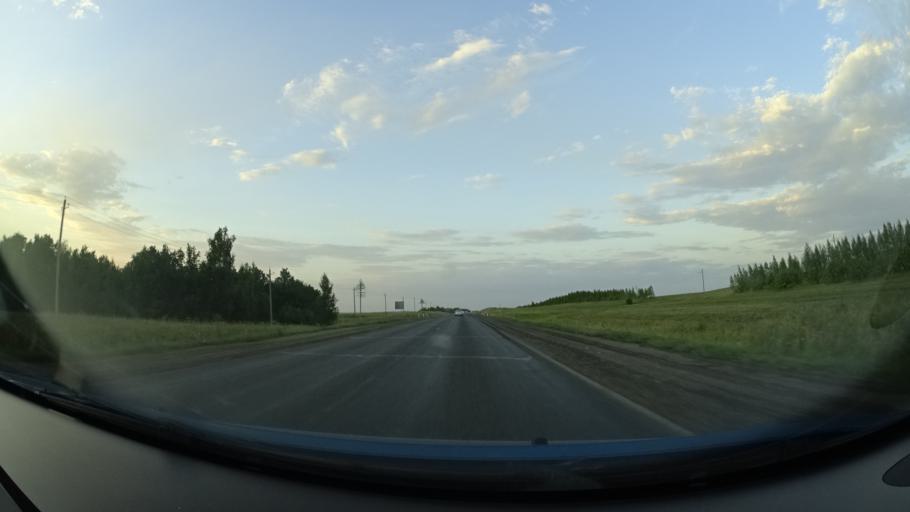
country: RU
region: Orenburg
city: Severnoye
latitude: 54.2003
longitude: 52.6885
